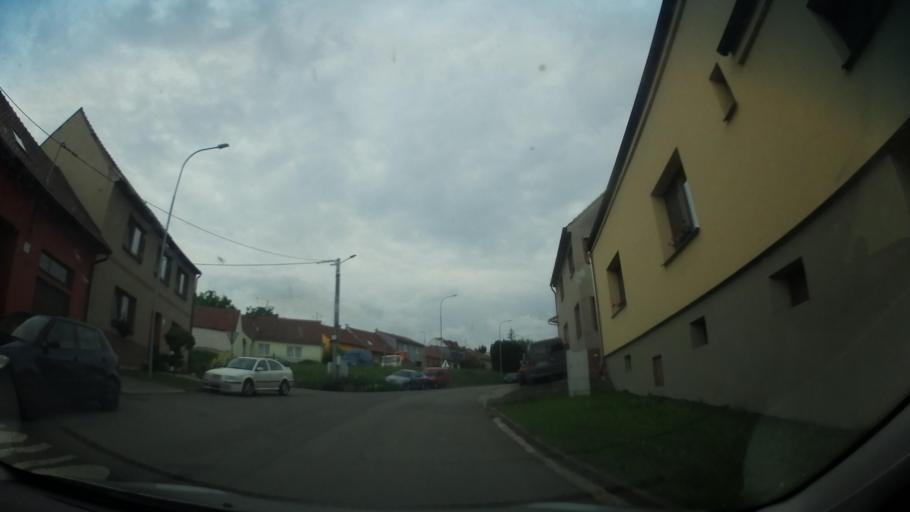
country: CZ
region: South Moravian
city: Cebin
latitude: 49.3122
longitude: 16.4810
